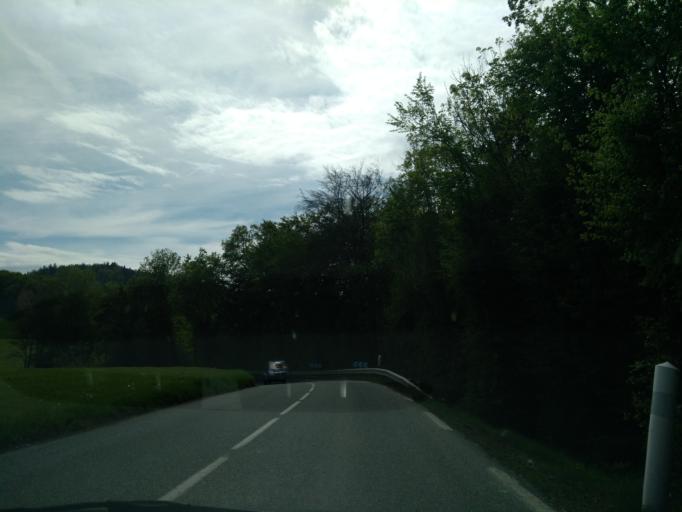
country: FR
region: Rhone-Alpes
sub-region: Departement de la Haute-Savoie
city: Chavanod
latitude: 45.8795
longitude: 6.0271
